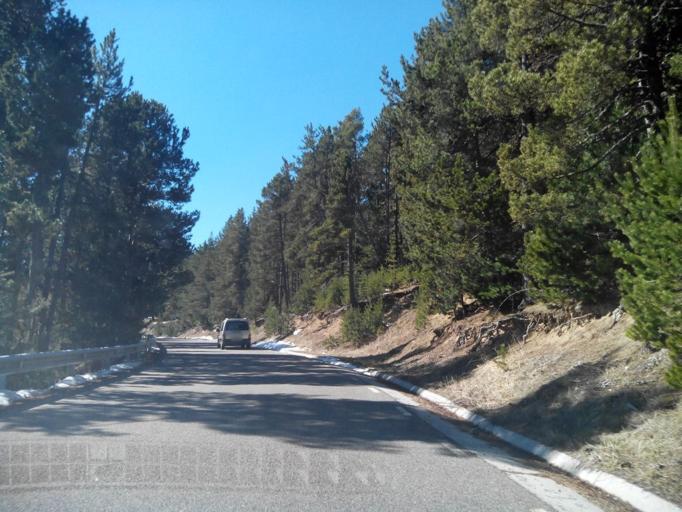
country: ES
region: Catalonia
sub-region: Provincia de Lleida
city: Lles de Cerdanya
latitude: 42.4226
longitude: 1.6700
